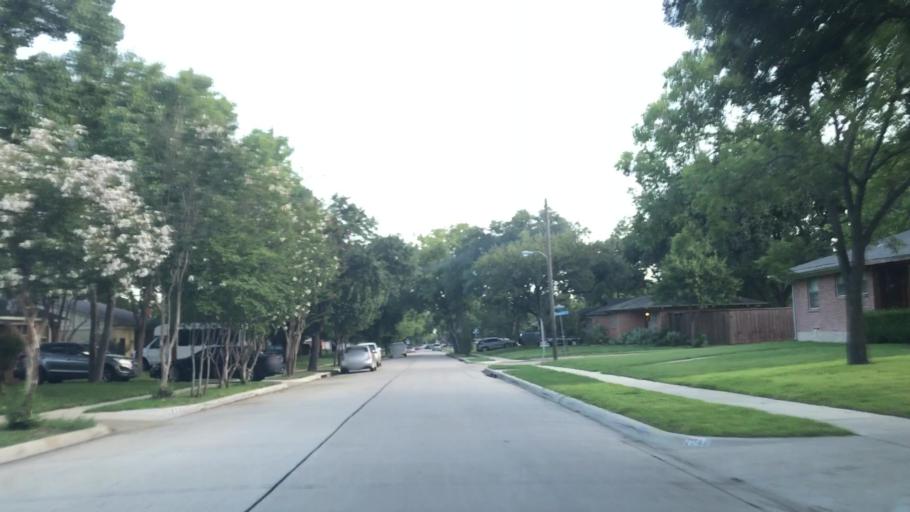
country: US
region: Texas
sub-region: Dallas County
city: Richardson
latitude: 32.9499
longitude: -96.7585
